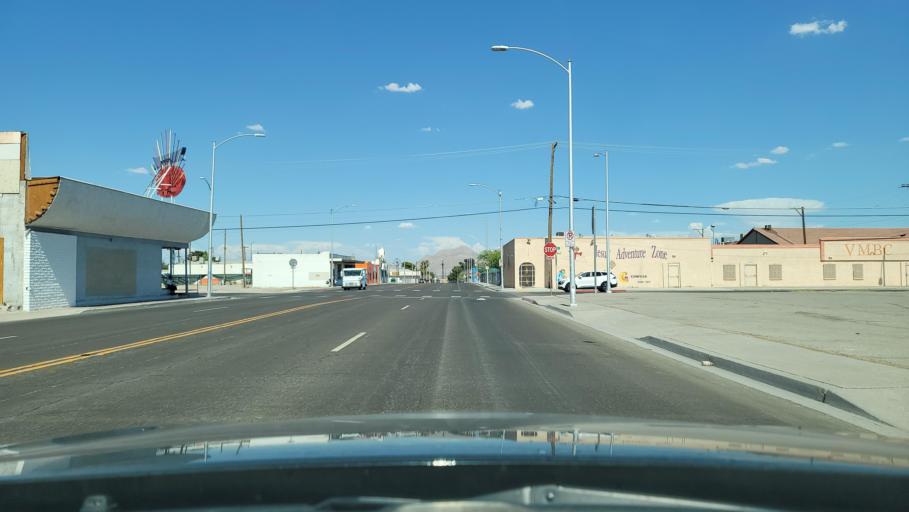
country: US
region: Nevada
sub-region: Clark County
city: Las Vegas
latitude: 36.1859
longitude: -115.1503
